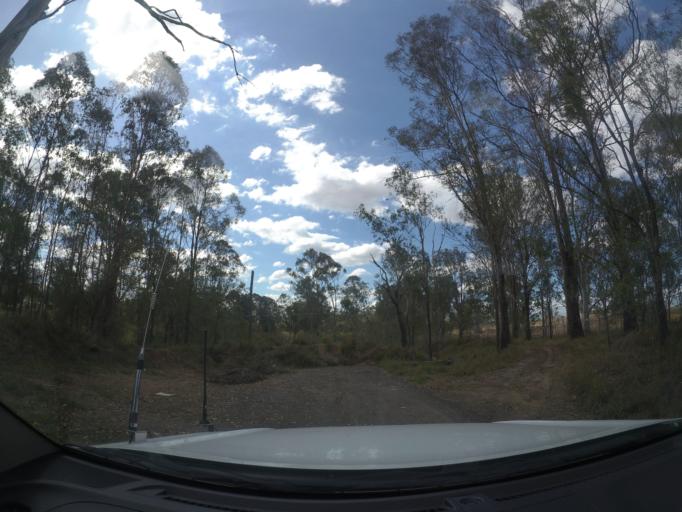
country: AU
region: Queensland
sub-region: Logan
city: North Maclean
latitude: -27.8203
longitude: 153.0055
